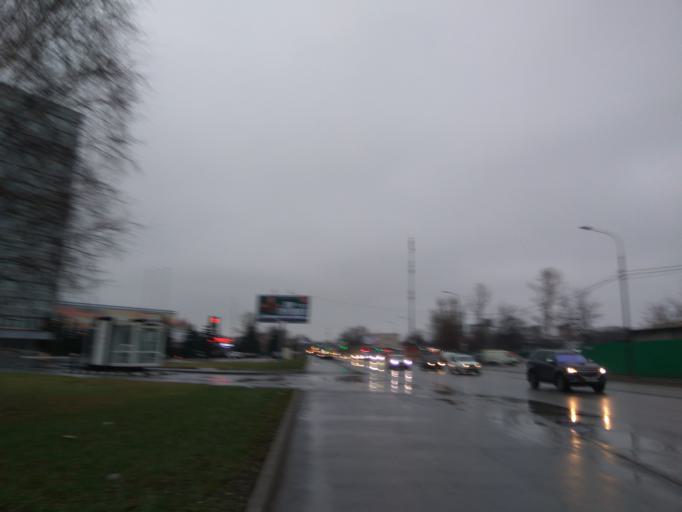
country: RU
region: Moscow
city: Tekstil'shchiki
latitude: 55.7058
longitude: 37.7269
